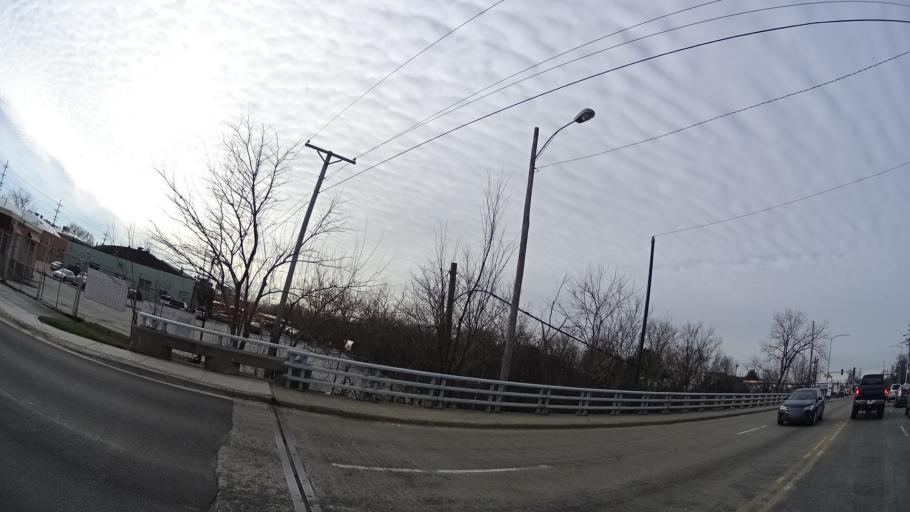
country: US
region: Illinois
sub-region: Cook County
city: Lincolnwood
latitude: 42.0191
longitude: -87.7098
